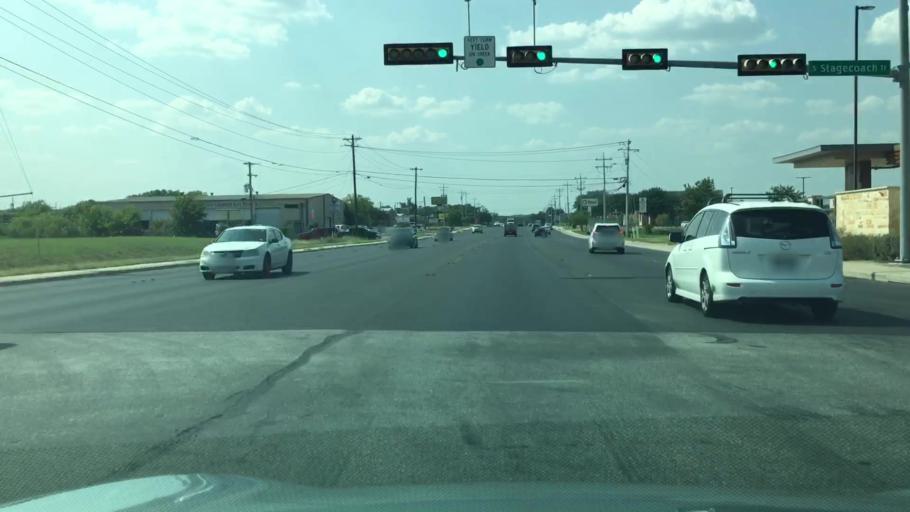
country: US
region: Texas
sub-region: Hays County
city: San Marcos
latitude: 29.8622
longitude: -97.9591
